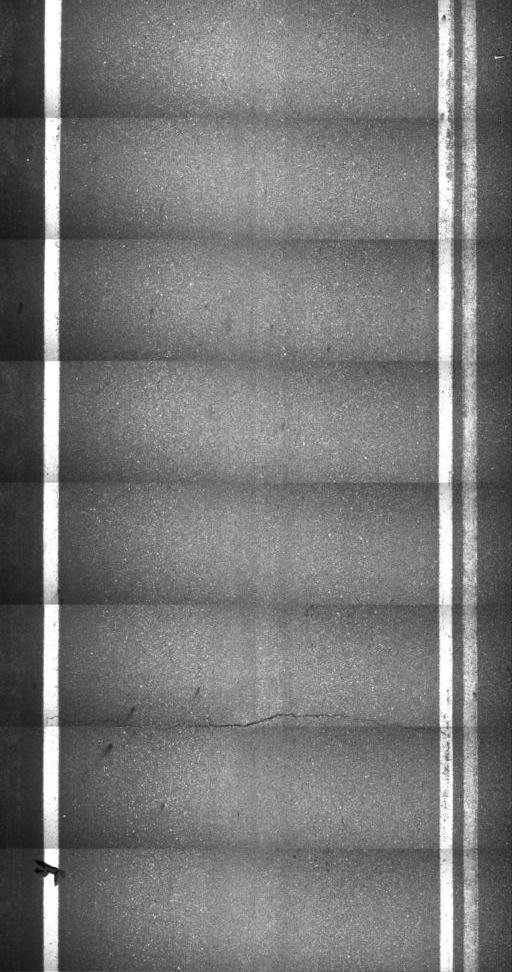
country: US
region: Vermont
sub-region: Washington County
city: Northfield
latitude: 44.0460
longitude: -72.6458
